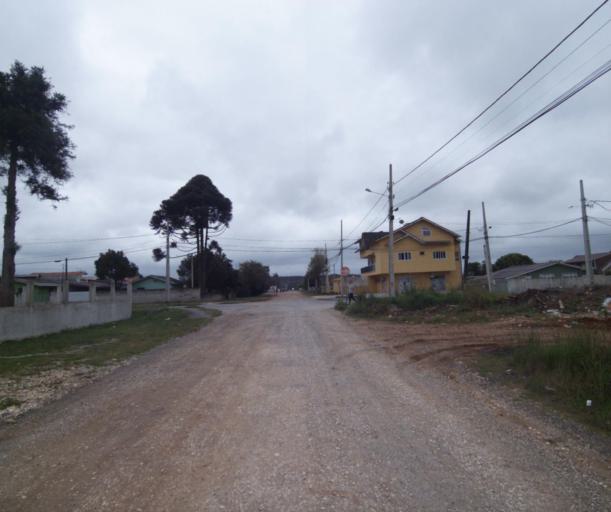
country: BR
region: Parana
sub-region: Quatro Barras
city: Quatro Barras
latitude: -25.3627
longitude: -49.0965
